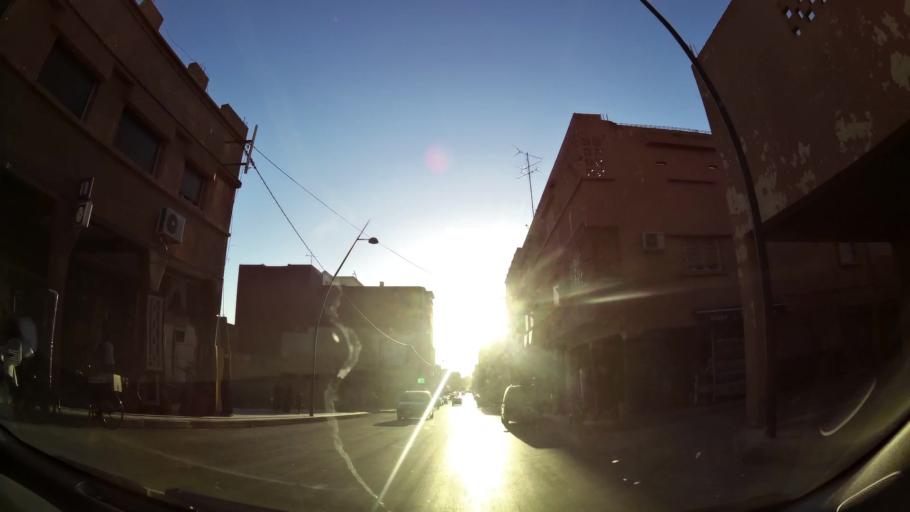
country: MA
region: Oriental
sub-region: Berkane-Taourirt
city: Berkane
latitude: 34.9205
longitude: -2.3275
